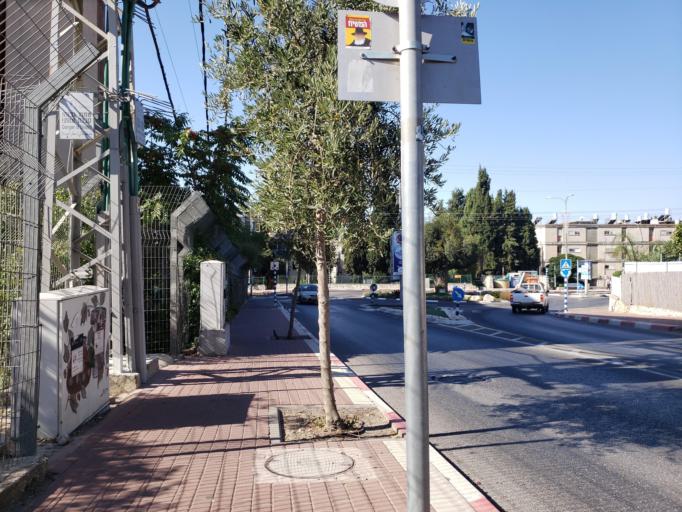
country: IL
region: Northern District
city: Safed
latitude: 32.9599
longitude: 35.4979
